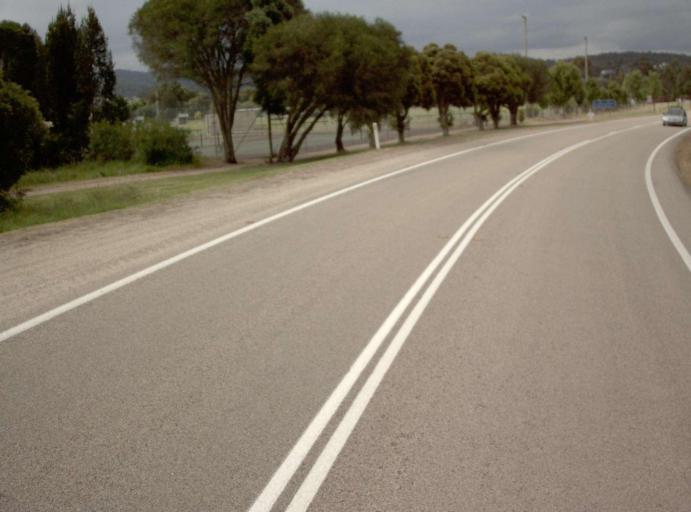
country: AU
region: Victoria
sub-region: East Gippsland
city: Lakes Entrance
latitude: -37.7144
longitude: 147.8363
